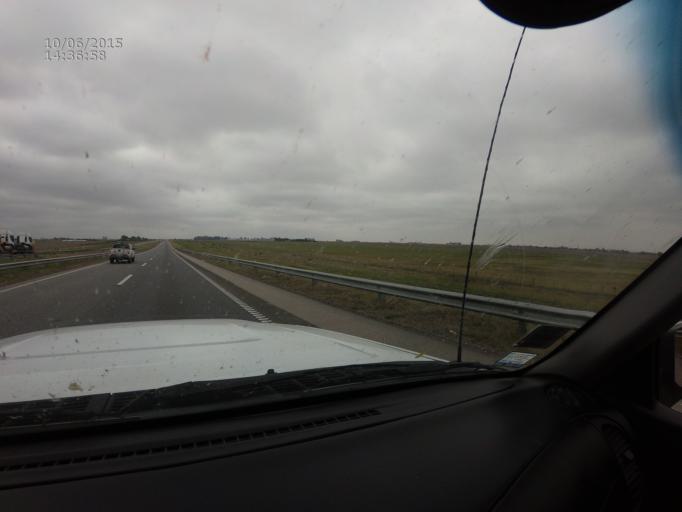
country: AR
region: Cordoba
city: James Craik
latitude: -32.1147
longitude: -63.4543
